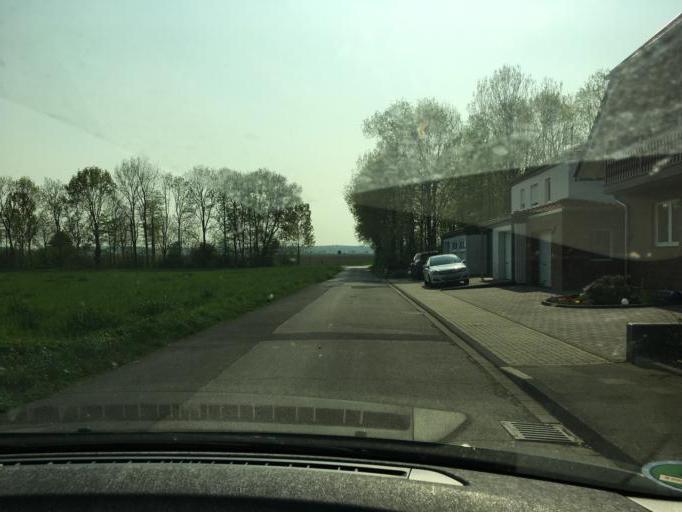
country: DE
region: North Rhine-Westphalia
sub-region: Regierungsbezirk Koln
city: Vettweiss
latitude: 50.7603
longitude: 6.5602
